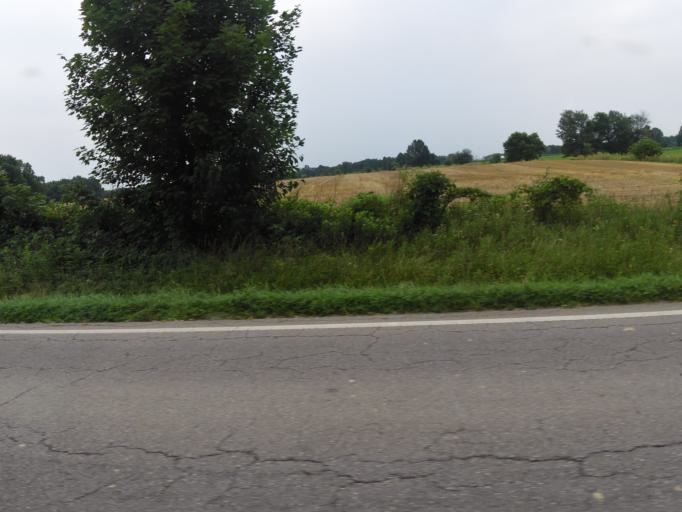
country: US
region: Ohio
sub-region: Clinton County
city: Blanchester
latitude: 39.2750
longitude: -83.9045
